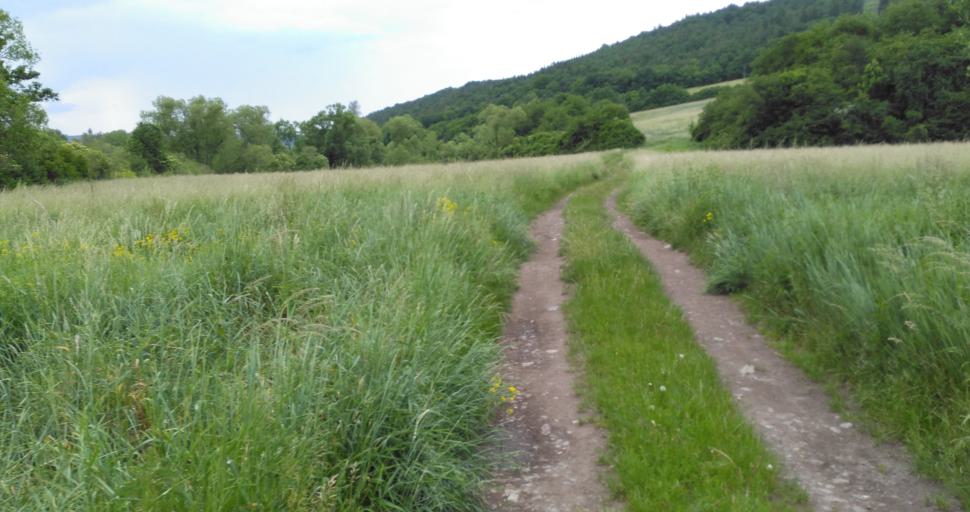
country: CZ
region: Central Bohemia
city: Jince
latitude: 49.7801
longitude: 13.9996
